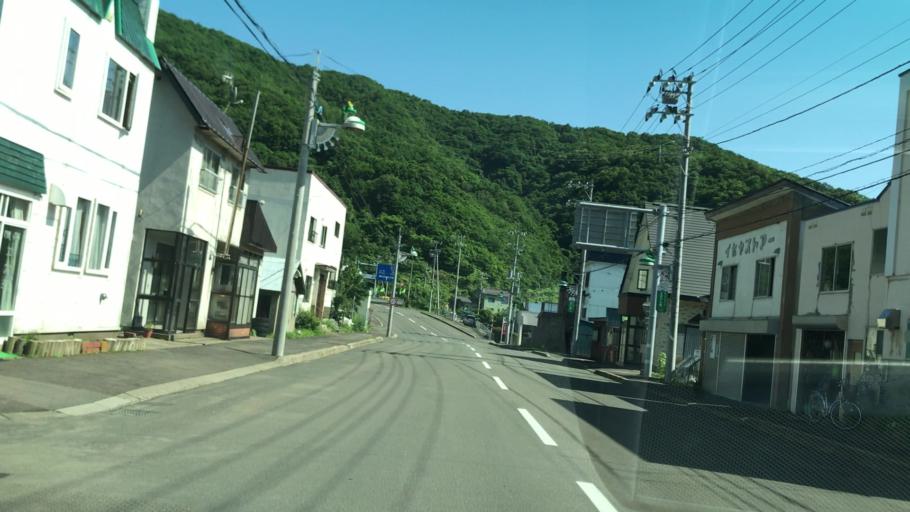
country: JP
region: Hokkaido
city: Iwanai
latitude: 43.1437
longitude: 140.4326
